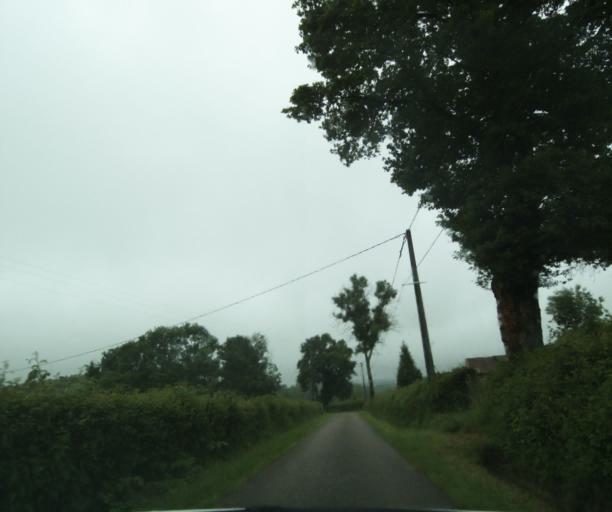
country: FR
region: Bourgogne
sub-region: Departement de Saone-et-Loire
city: Charolles
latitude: 46.4096
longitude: 4.1979
